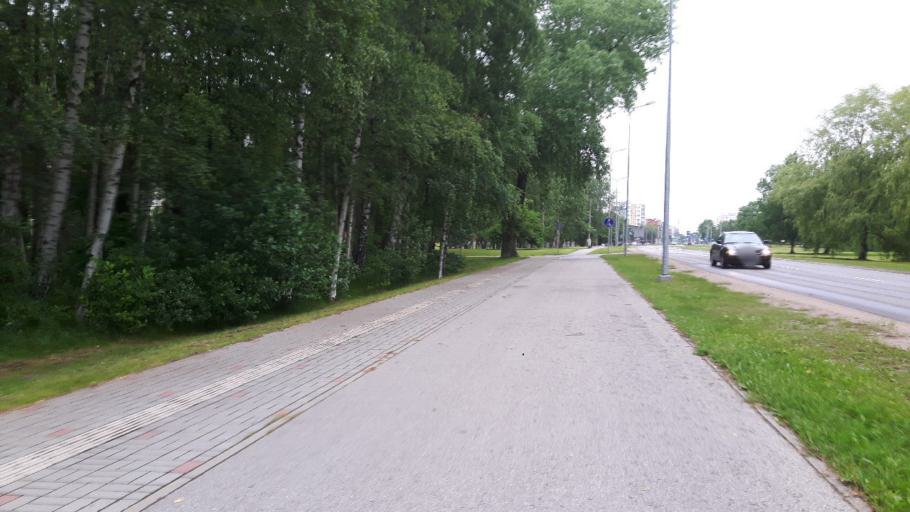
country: LV
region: Liepaja
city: Liepaja
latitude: 56.4831
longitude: 21.0064
